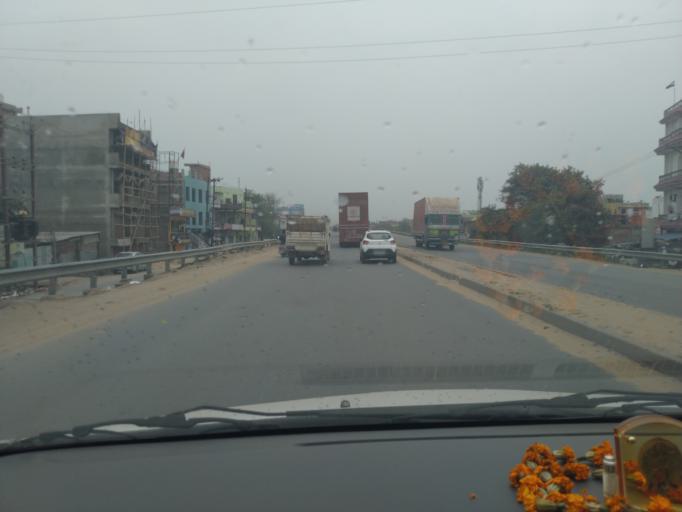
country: IN
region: Bihar
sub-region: Rohtas
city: Dehri
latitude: 24.9087
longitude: 84.1814
